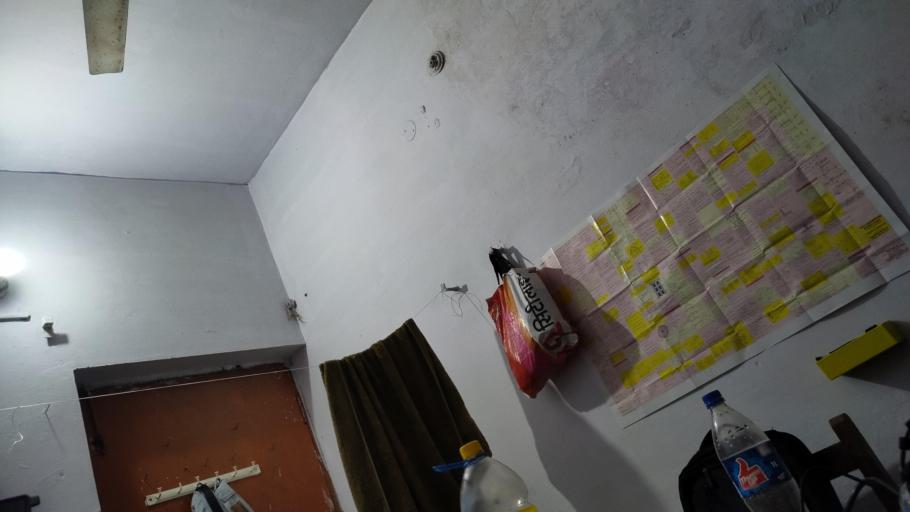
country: IN
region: Uttar Pradesh
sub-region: Allahabad
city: Allahabad
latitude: 25.4897
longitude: 81.8641
